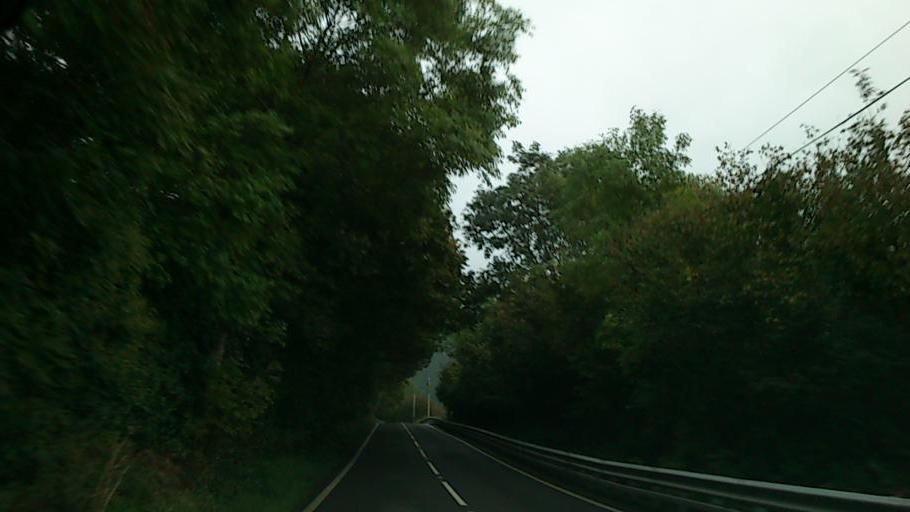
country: GB
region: Wales
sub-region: Gwynedd
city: Corris
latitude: 52.6981
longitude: -3.6366
